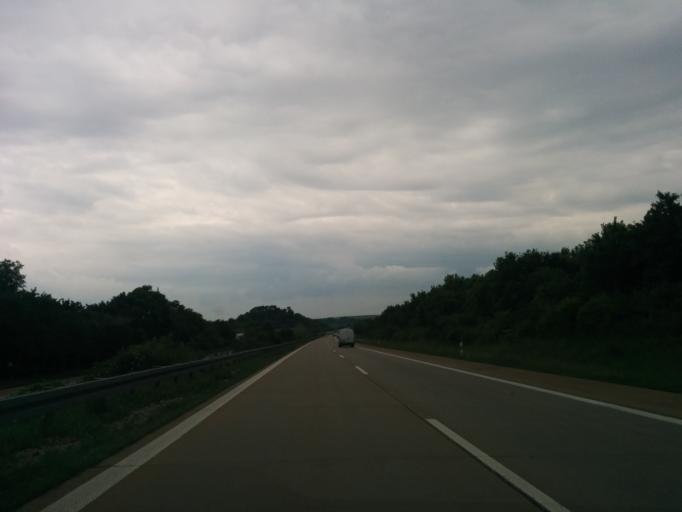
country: DE
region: Bavaria
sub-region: Regierungsbezirk Mittelfranken
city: Diebach
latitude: 49.2894
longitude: 10.2211
